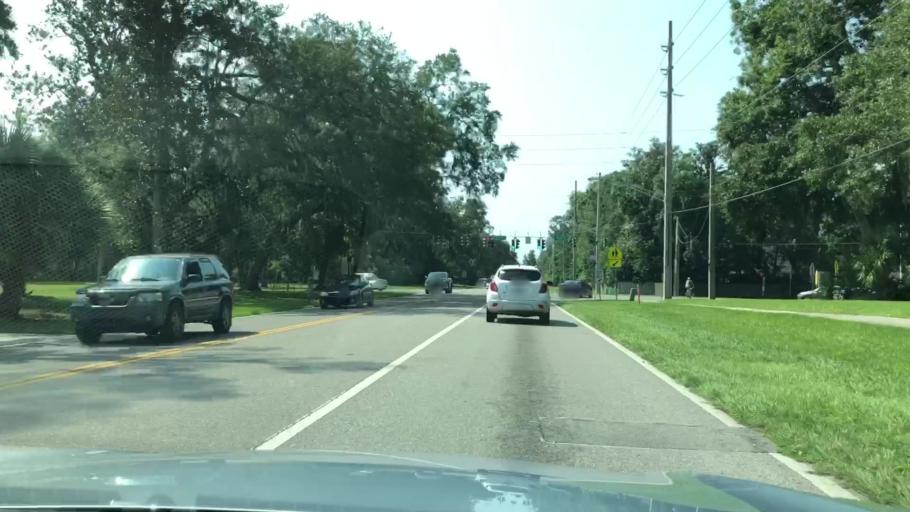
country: US
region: Florida
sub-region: Duval County
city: Neptune Beach
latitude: 30.3157
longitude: -81.4079
